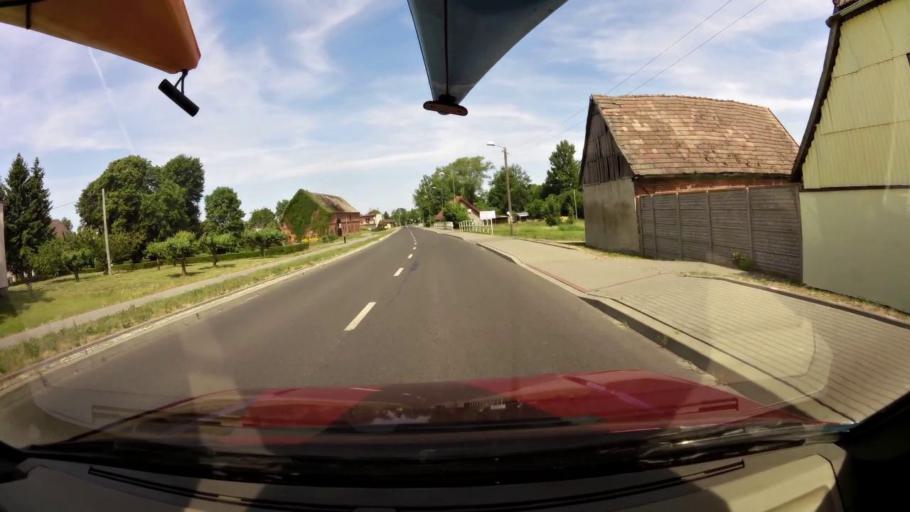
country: PL
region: West Pomeranian Voivodeship
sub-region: Powiat koszalinski
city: Sianow
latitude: 54.3114
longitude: 16.3070
